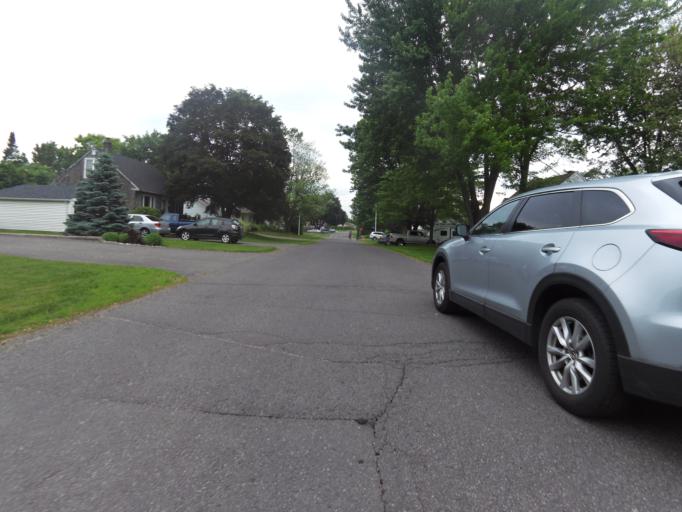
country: CA
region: Ontario
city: Ottawa
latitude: 45.3512
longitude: -75.7463
